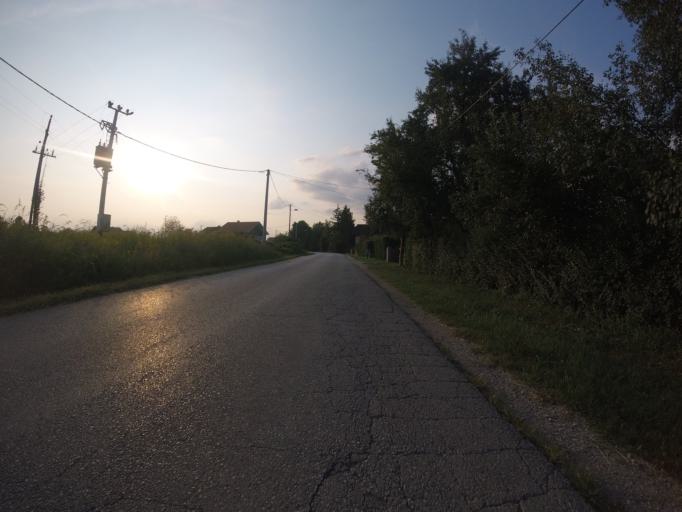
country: HR
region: Zagrebacka
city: Micevec
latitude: 45.7504
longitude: 16.1339
